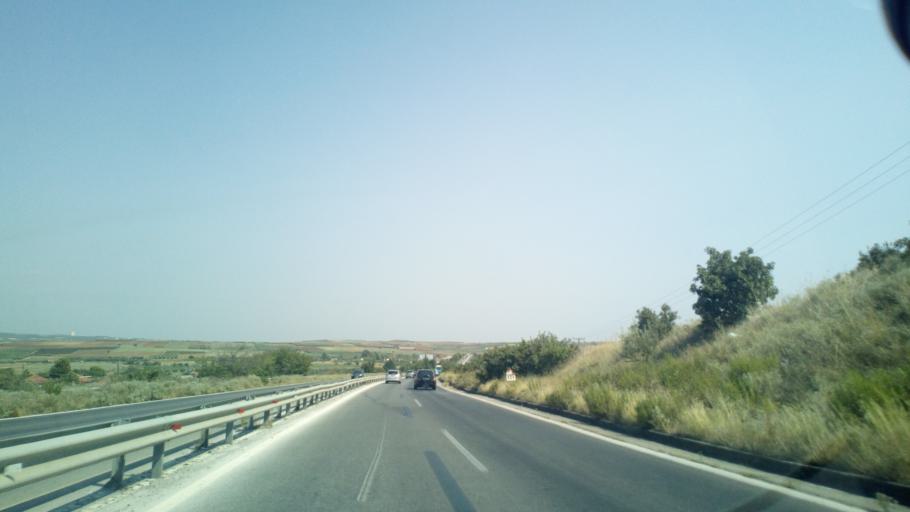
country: GR
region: Central Macedonia
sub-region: Nomos Chalkidikis
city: Nea Kallikrateia
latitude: 40.3122
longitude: 23.1107
